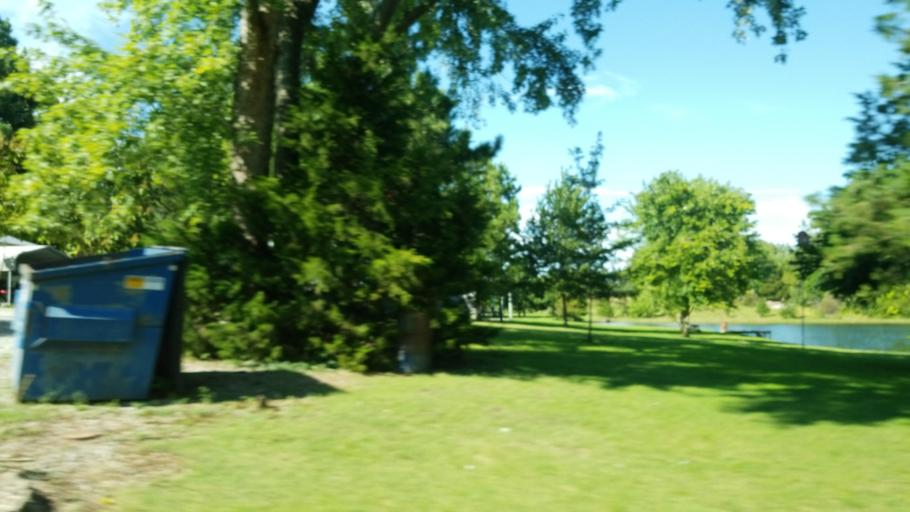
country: US
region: Illinois
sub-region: Saline County
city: Carrier Mills
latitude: 37.7960
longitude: -88.6481
